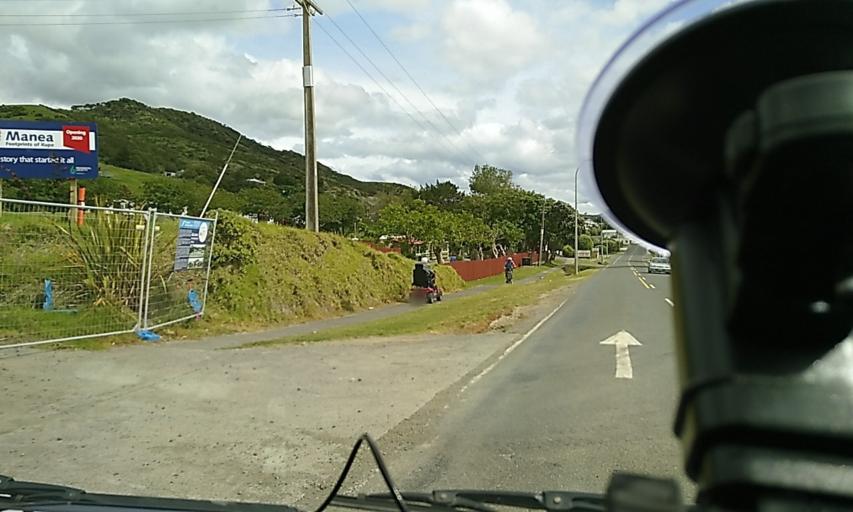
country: NZ
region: Northland
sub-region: Far North District
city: Ahipara
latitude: -35.5076
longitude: 173.3902
